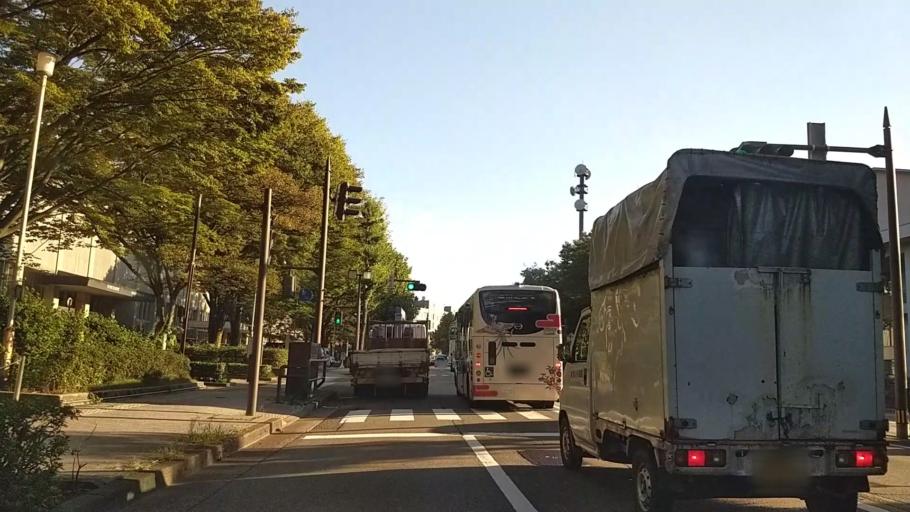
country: JP
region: Ishikawa
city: Kanazawa-shi
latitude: 36.5598
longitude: 136.6593
